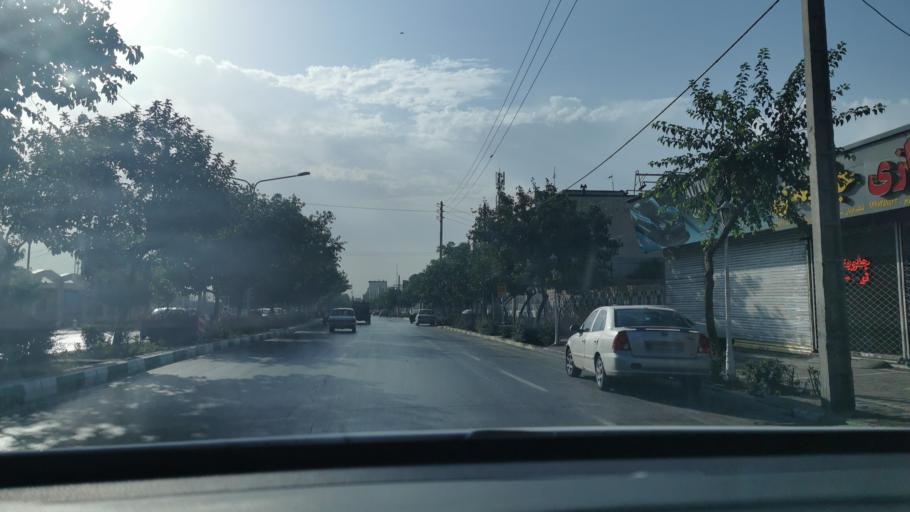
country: IR
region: Razavi Khorasan
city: Mashhad
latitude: 36.2894
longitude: 59.6525
